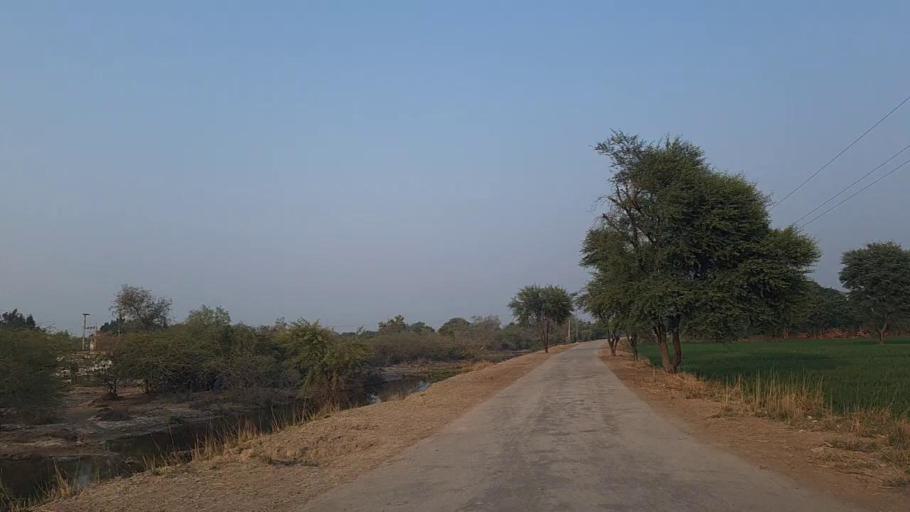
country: PK
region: Sindh
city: Nawabshah
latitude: 26.2462
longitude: 68.4625
